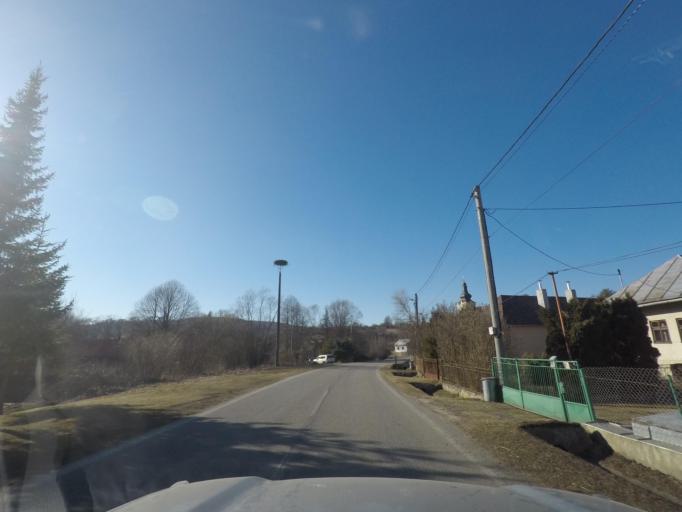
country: PL
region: Subcarpathian Voivodeship
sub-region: Powiat sanocki
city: Komancza
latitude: 49.1636
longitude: 22.0408
